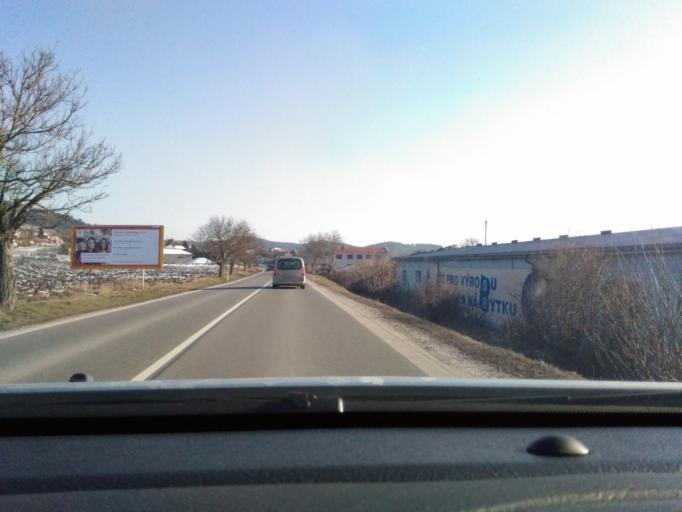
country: CZ
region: South Moravian
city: Cebin
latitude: 49.3216
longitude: 16.4654
